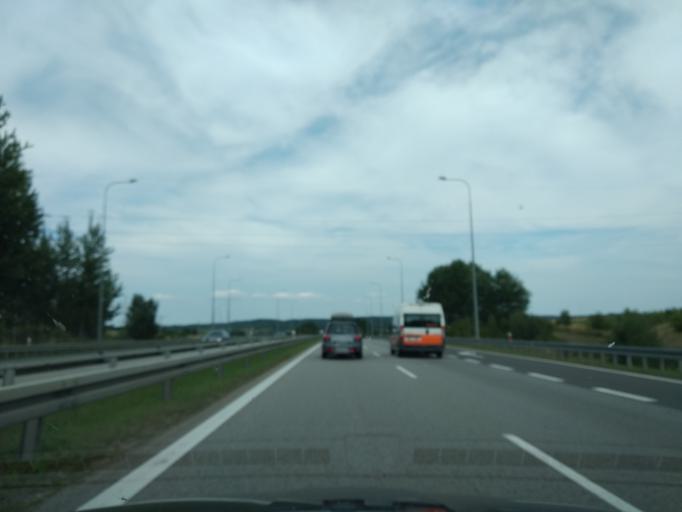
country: PL
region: West Pomeranian Voivodeship
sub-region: Szczecin
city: Szczecin
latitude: 53.3374
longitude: 14.5597
